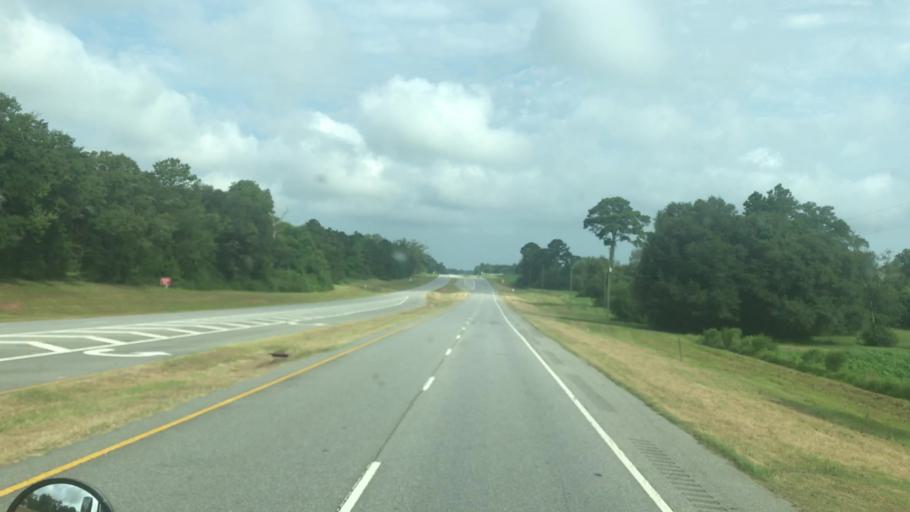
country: US
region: Georgia
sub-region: Miller County
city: Colquitt
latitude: 31.2505
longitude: -84.7982
